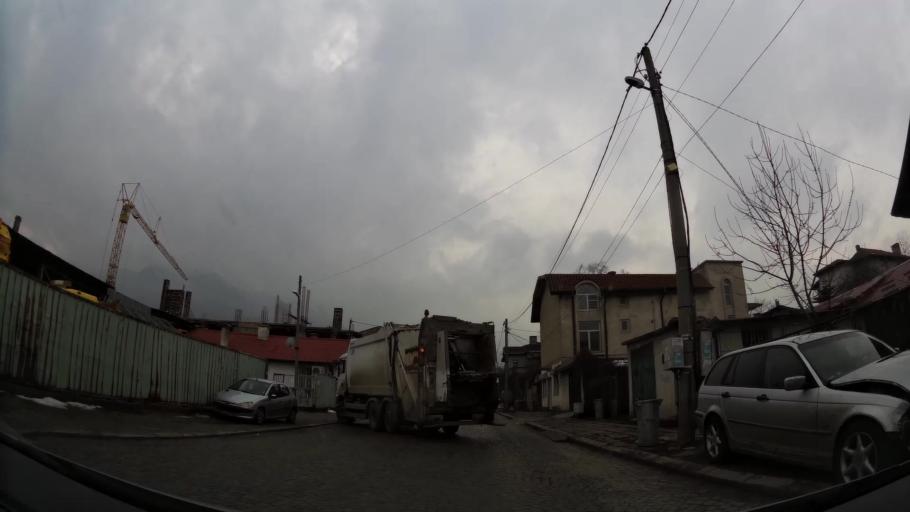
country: BG
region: Sofia-Capital
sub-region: Stolichna Obshtina
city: Sofia
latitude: 42.6614
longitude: 23.2438
